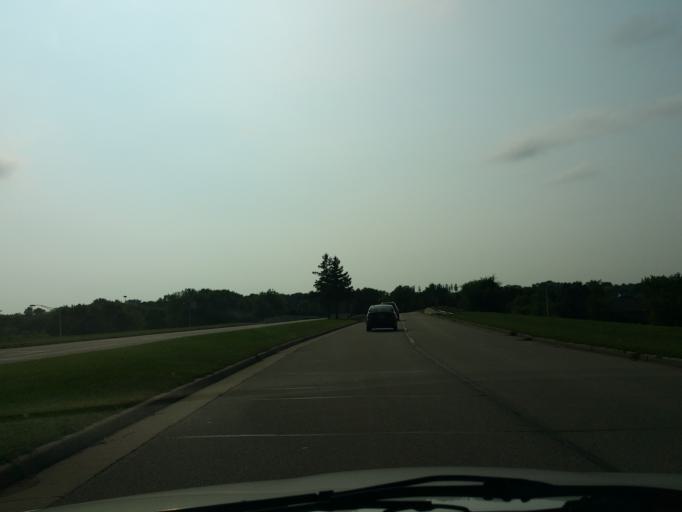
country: US
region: Wisconsin
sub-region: Saint Croix County
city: Hudson
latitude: 44.9490
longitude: -92.7258
